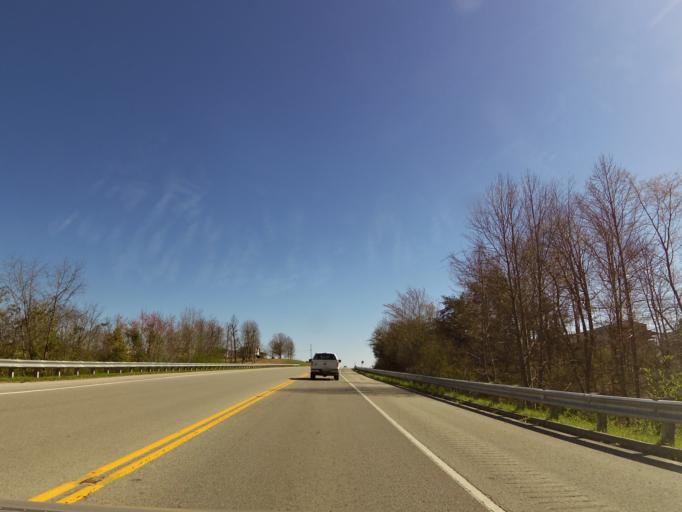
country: US
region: Kentucky
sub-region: McCreary County
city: Pine Knot
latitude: 36.6470
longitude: -84.4342
